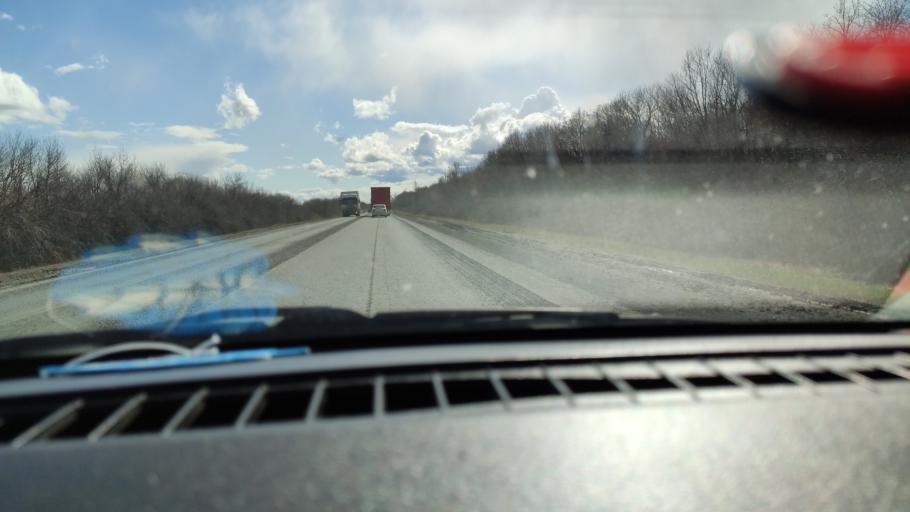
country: RU
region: Saratov
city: Dukhovnitskoye
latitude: 52.6421
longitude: 48.1927
